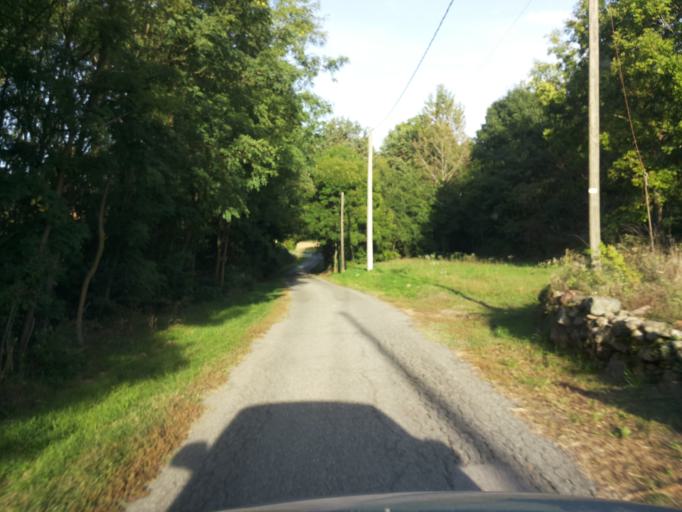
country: IT
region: Piedmont
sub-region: Provincia di Biella
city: Salussola
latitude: 45.4471
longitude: 8.0976
